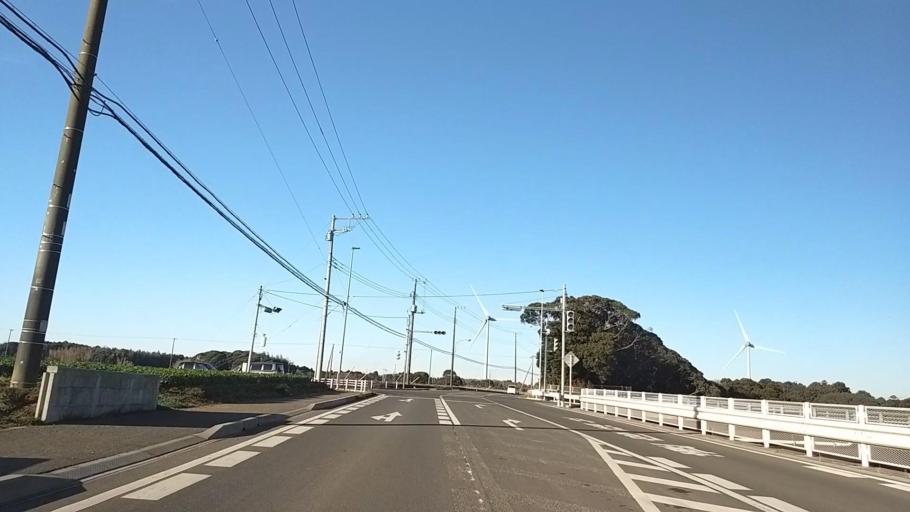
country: JP
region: Chiba
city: Hasaki
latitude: 35.7520
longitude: 140.7397
